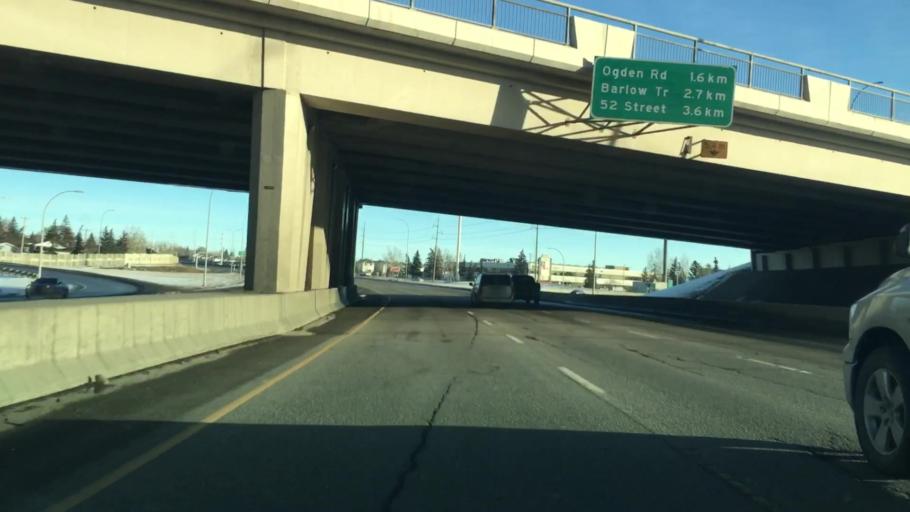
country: CA
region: Alberta
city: Calgary
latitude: 50.9807
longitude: -114.0162
